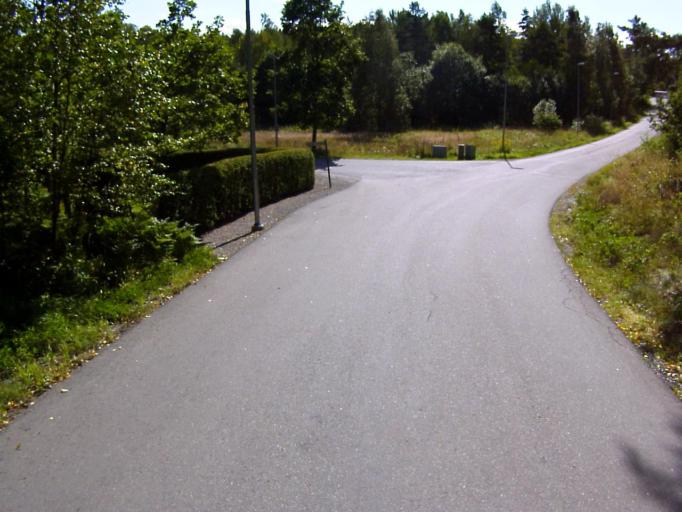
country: SE
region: Soedermanland
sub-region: Eskilstuna Kommun
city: Eskilstuna
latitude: 59.3585
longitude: 16.5585
